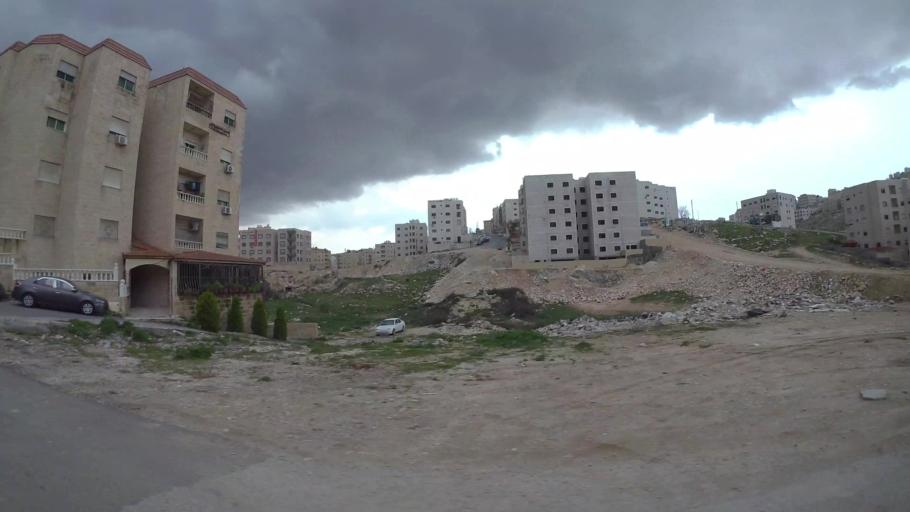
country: JO
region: Amman
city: Amman
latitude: 32.0086
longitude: 35.9466
